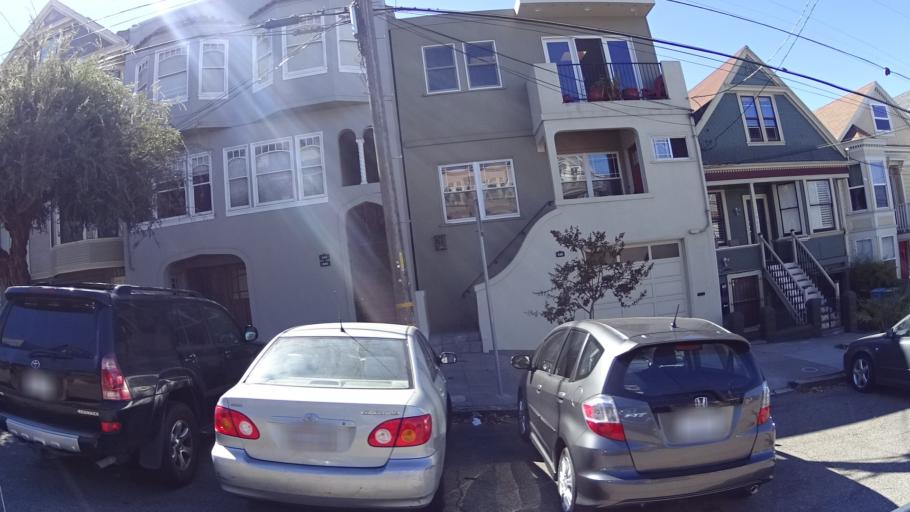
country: US
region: California
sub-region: San Francisco County
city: San Francisco
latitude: 37.7627
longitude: -122.4044
